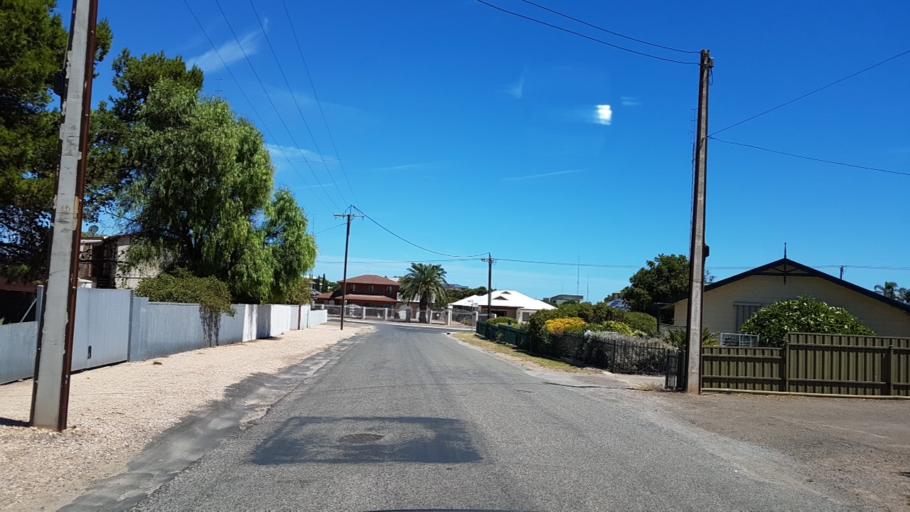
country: AU
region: South Australia
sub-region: Copper Coast
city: Wallaroo
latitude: -34.0588
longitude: 137.5607
